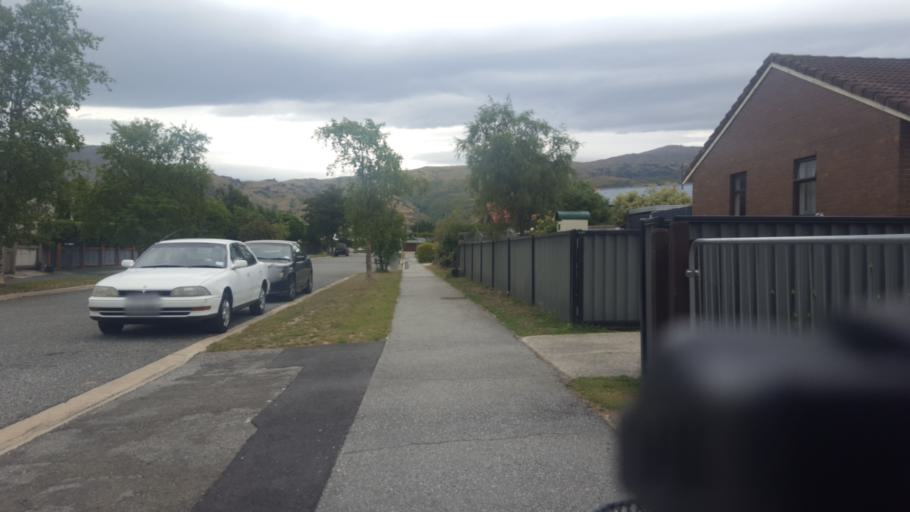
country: NZ
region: Otago
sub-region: Queenstown-Lakes District
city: Wanaka
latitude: -45.0439
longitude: 169.1848
